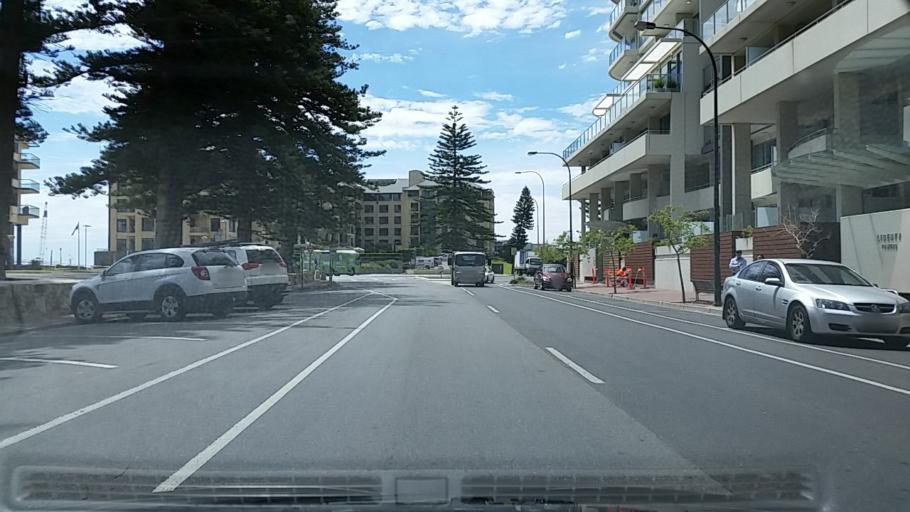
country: AU
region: South Australia
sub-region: Adelaide
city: Glenelg
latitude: -34.9775
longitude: 138.5122
